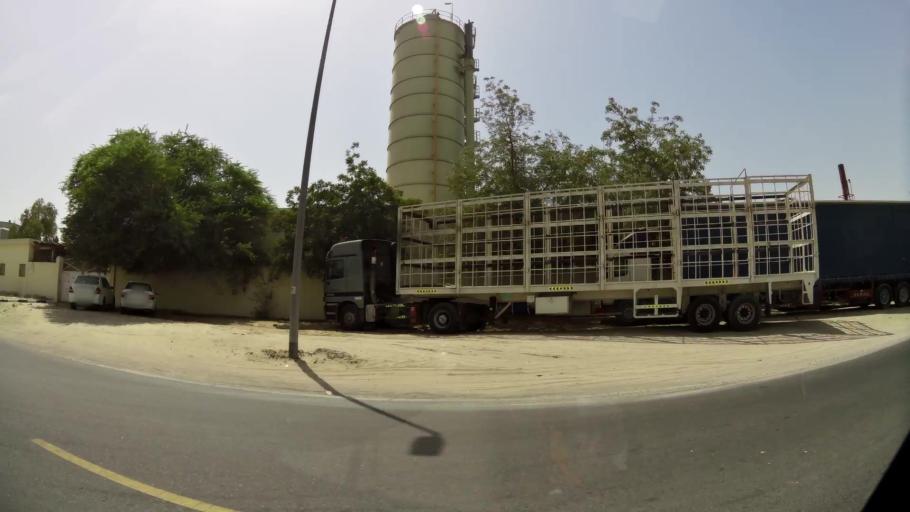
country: AE
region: Dubai
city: Dubai
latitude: 25.1406
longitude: 55.2352
